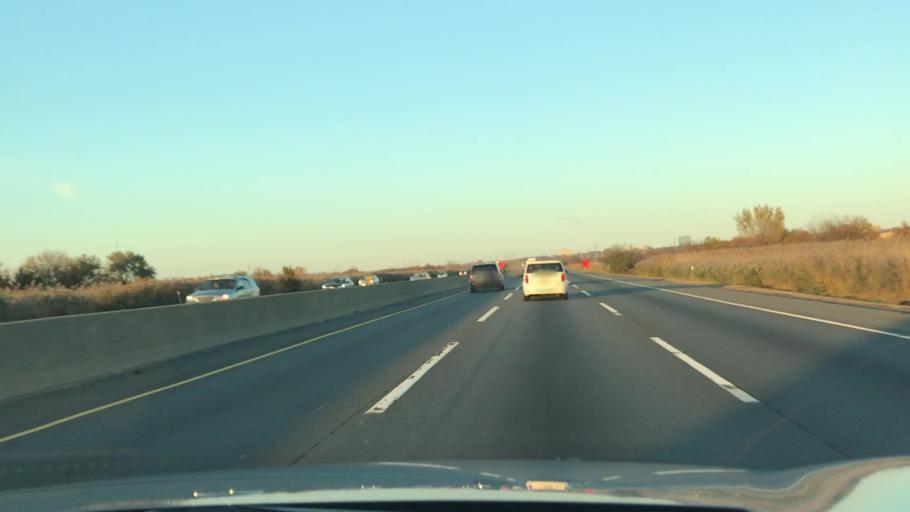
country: US
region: New Jersey
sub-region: Hudson County
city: Secaucus
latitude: 40.7941
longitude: -74.0433
